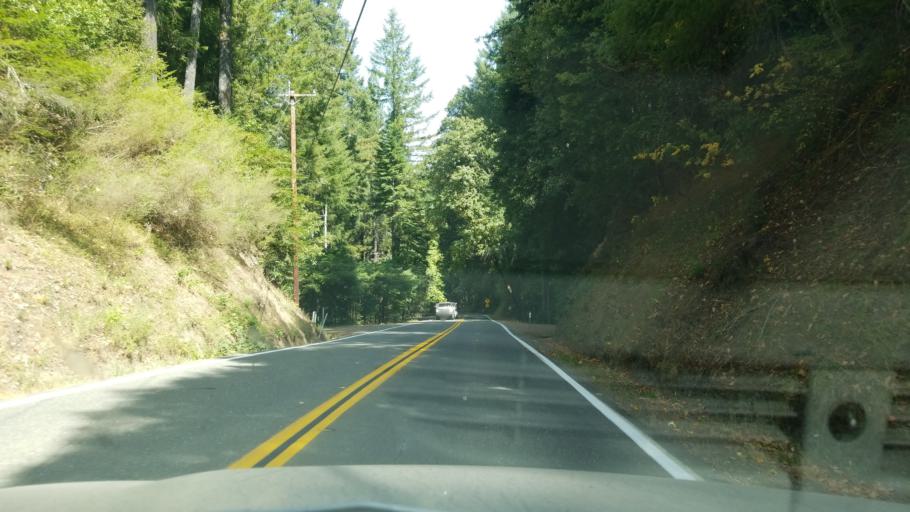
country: US
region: California
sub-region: Humboldt County
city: Redway
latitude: 39.8537
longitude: -123.7185
